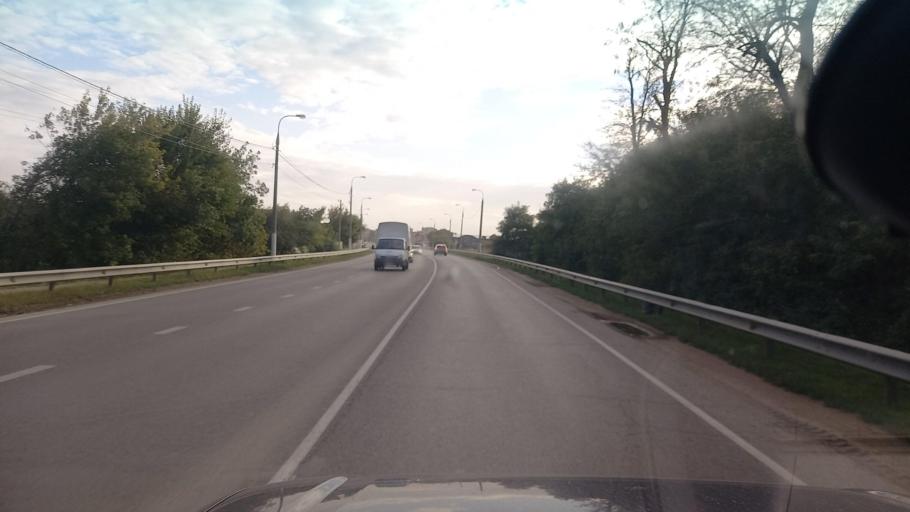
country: RU
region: Krasnodarskiy
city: Krasnodar
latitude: 45.1056
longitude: 38.9181
